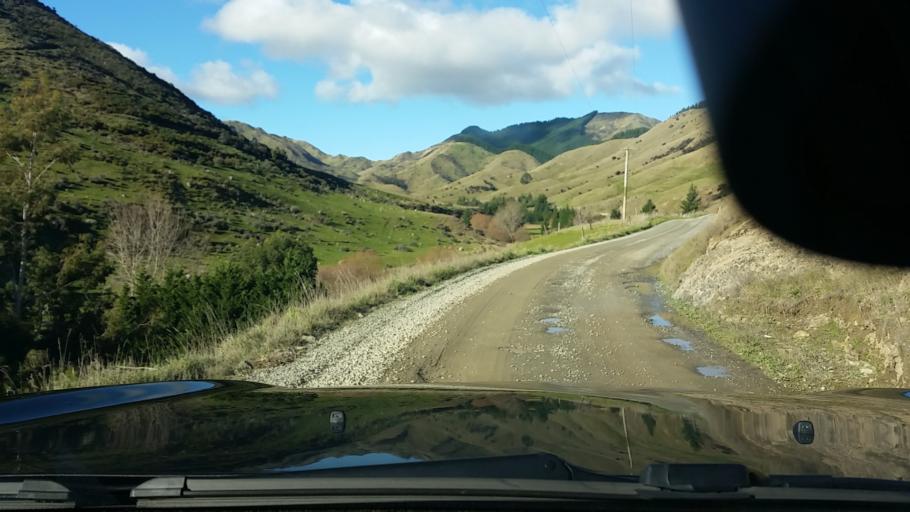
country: NZ
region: Marlborough
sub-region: Marlborough District
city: Blenheim
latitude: -41.6010
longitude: 173.9539
